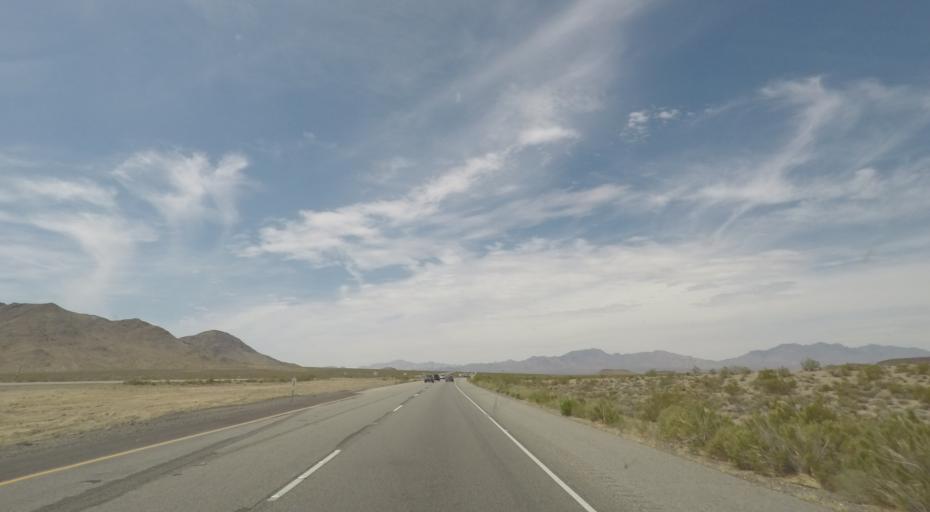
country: US
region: California
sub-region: San Bernardino County
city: Needles
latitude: 34.8014
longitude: -115.3213
